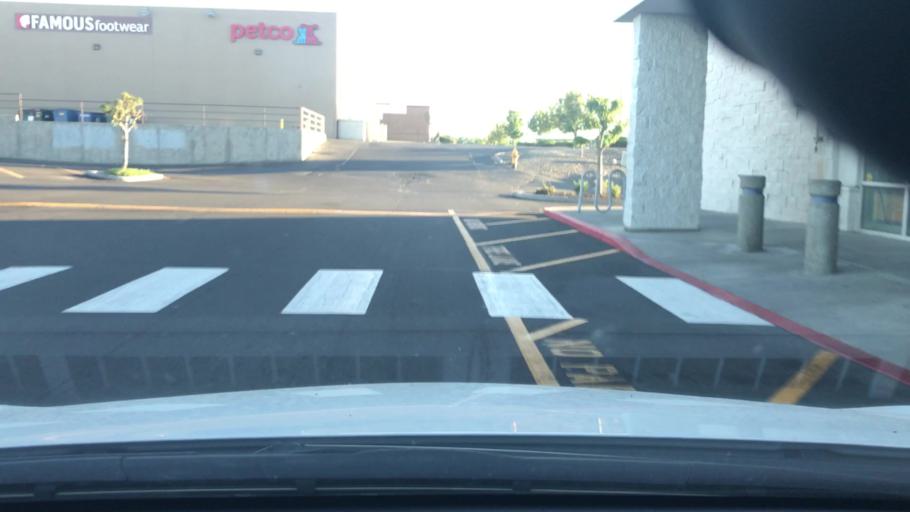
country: US
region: Washington
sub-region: Grant County
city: Moses Lake
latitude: 47.1398
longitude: -119.2769
